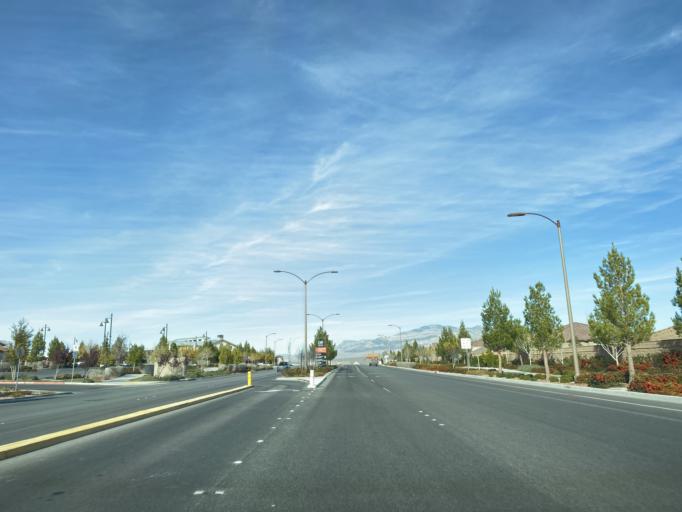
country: US
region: Nevada
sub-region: Clark County
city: Summerlin South
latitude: 36.3119
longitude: -115.3149
